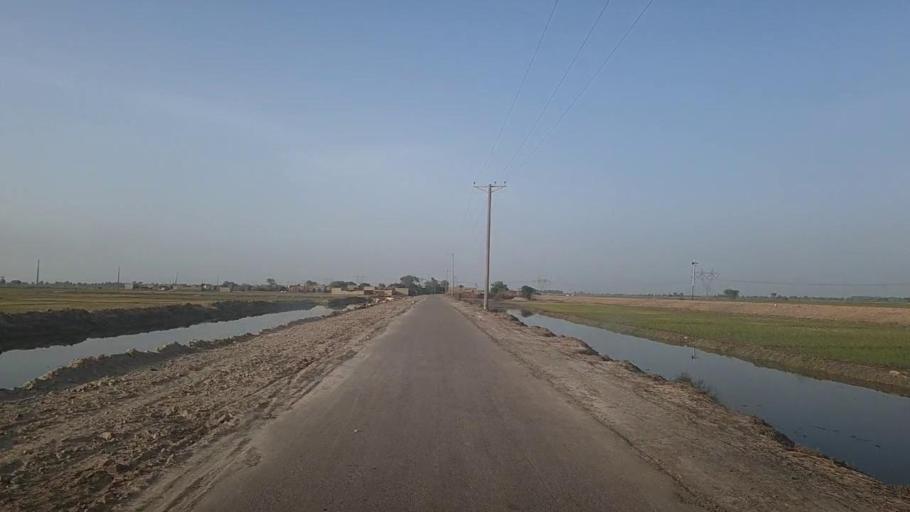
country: PK
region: Sindh
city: Radhan
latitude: 27.1150
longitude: 67.9129
